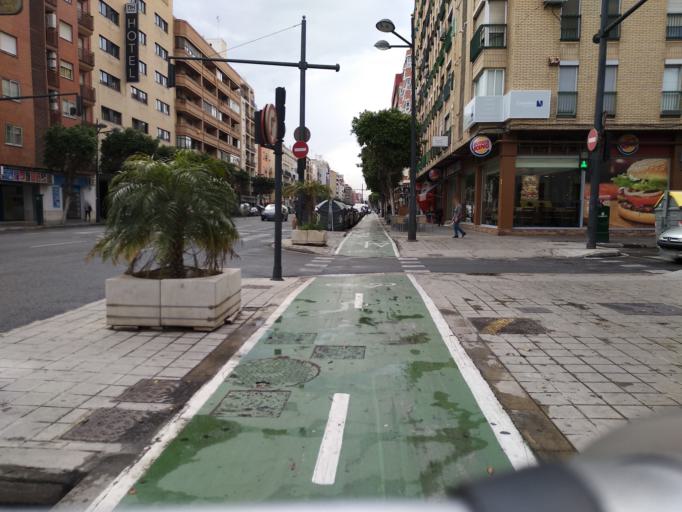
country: ES
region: Valencia
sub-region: Provincia de Valencia
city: Valencia
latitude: 39.4630
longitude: -0.3425
